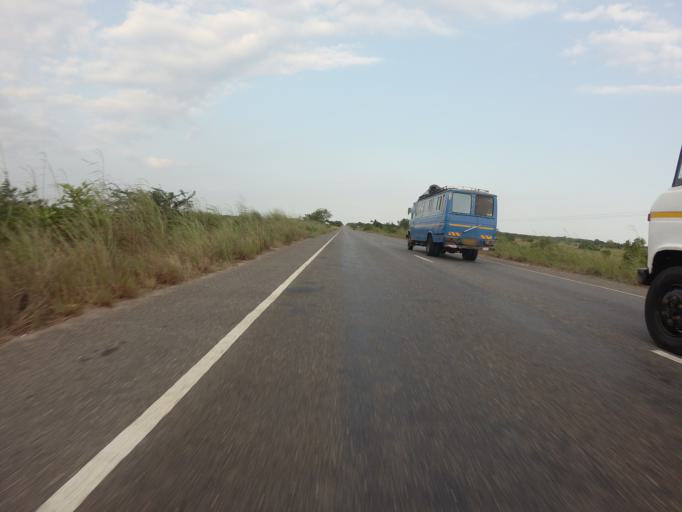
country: GH
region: Volta
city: Anloga
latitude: 6.0892
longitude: 0.5354
